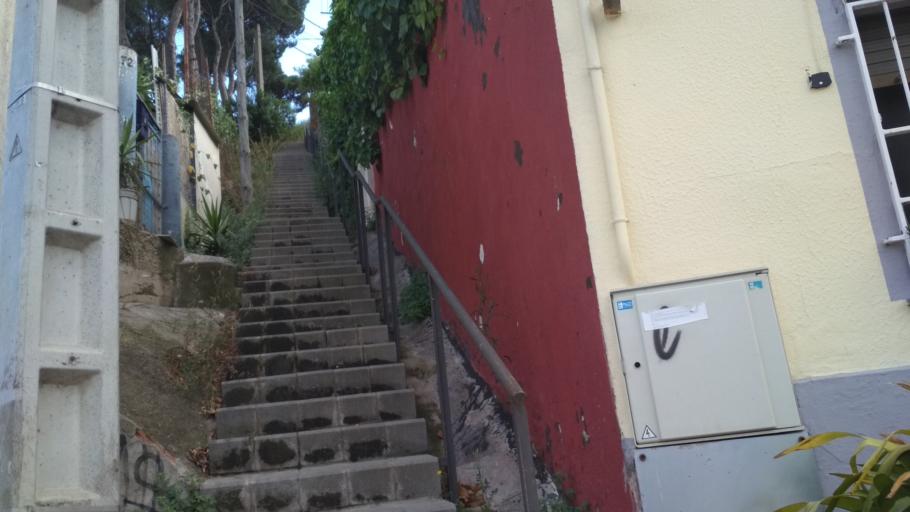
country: ES
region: Catalonia
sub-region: Provincia de Barcelona
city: Montcada i Reixac
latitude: 41.4690
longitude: 2.1846
